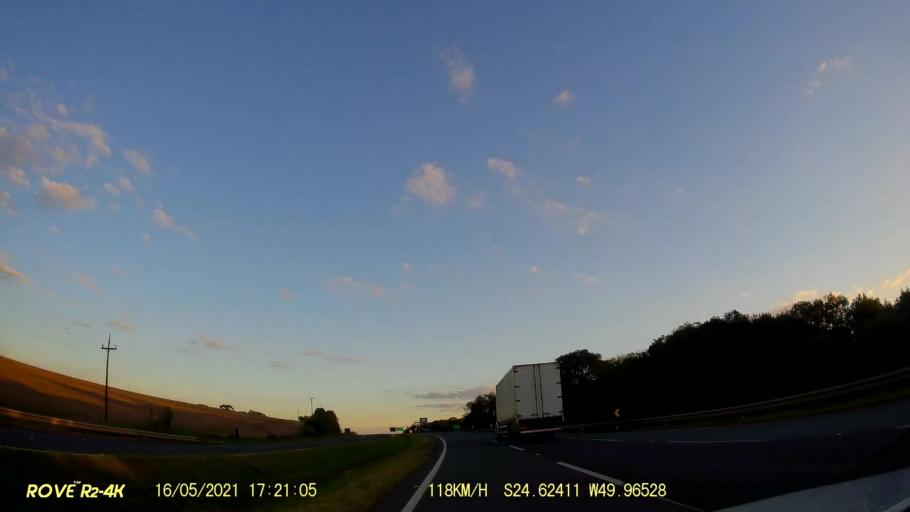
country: BR
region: Parana
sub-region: Pirai Do Sul
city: Pirai do Sul
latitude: -24.6245
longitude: -49.9655
